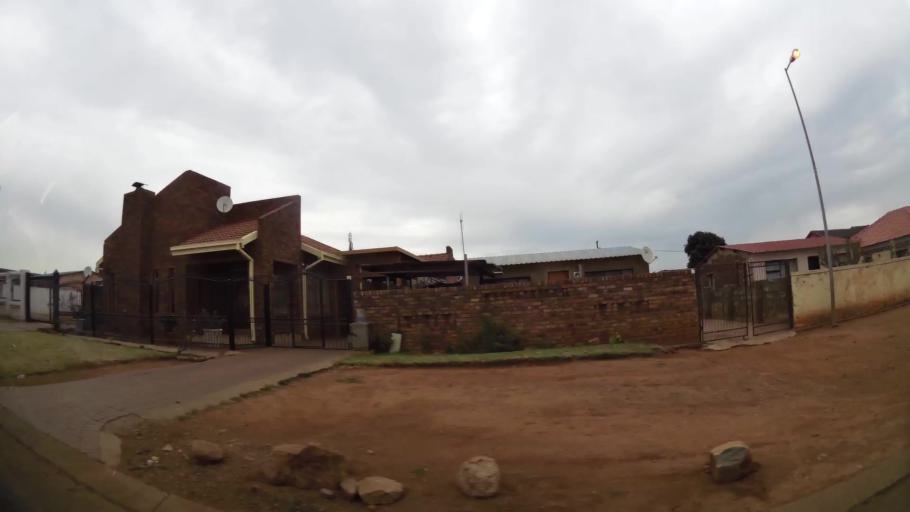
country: ZA
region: Gauteng
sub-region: City of Tshwane Metropolitan Municipality
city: Cullinan
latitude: -25.7084
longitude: 28.3631
